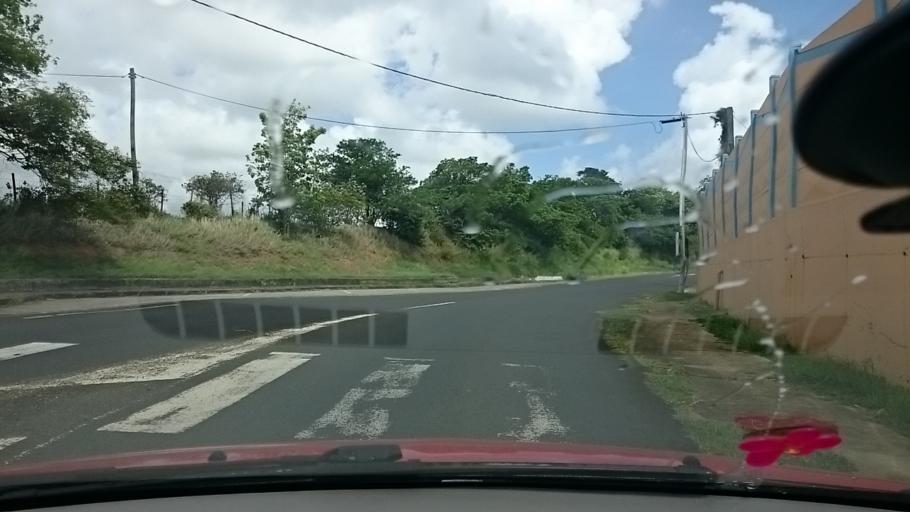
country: MQ
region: Martinique
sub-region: Martinique
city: La Trinite
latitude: 14.7550
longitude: -60.9246
